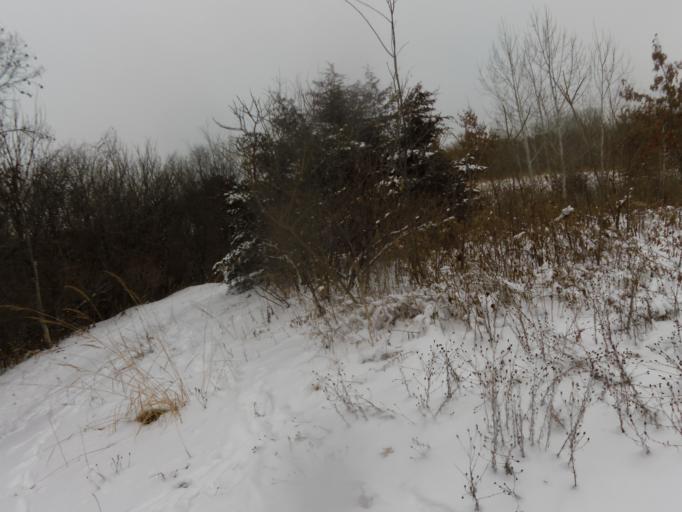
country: US
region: Minnesota
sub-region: Dakota County
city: Inver Grove Heights
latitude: 44.8574
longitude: -93.0753
